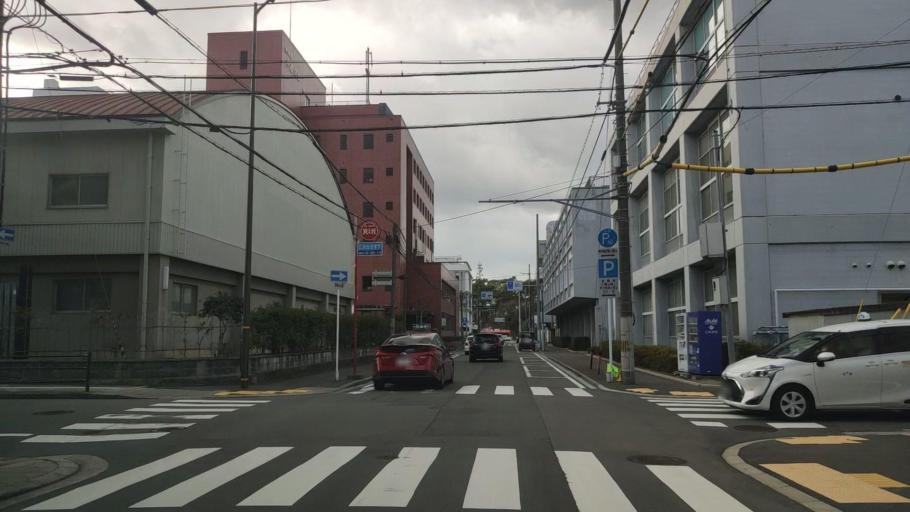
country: JP
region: Ehime
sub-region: Shikoku-chuo Shi
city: Matsuyama
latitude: 33.8402
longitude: 132.7671
